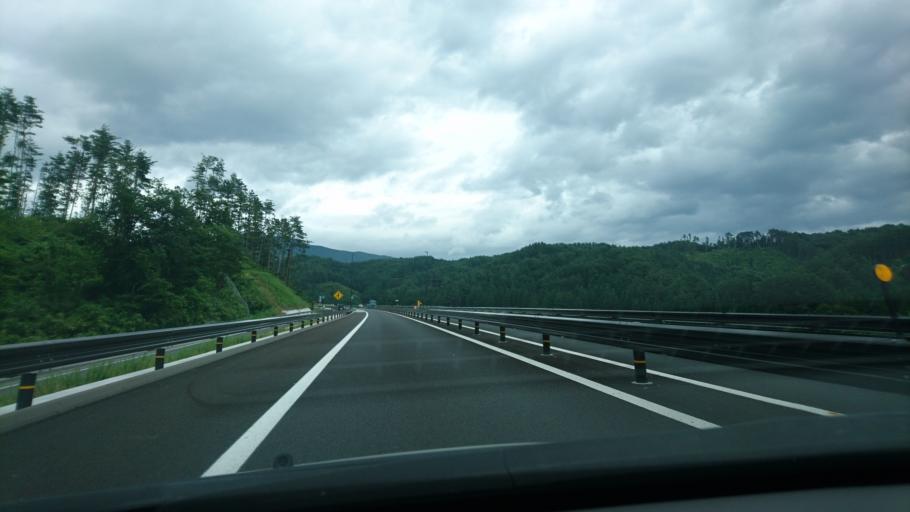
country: JP
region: Iwate
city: Yamada
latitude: 39.4818
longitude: 141.9505
